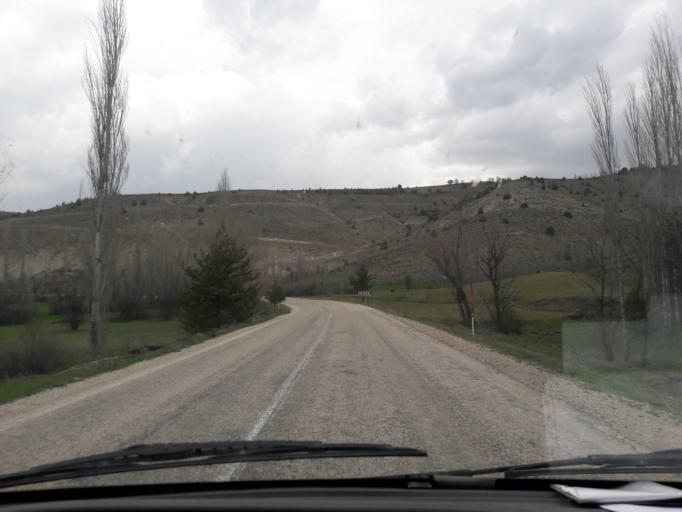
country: TR
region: Giresun
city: Alucra
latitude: 40.2850
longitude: 38.8194
